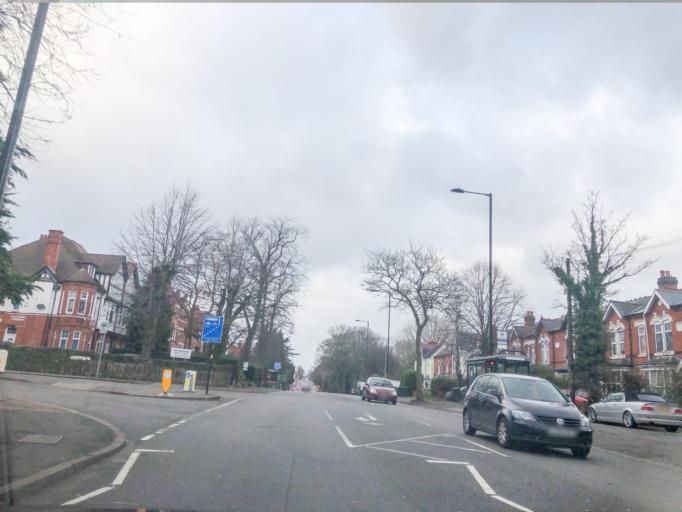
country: GB
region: England
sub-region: City and Borough of Birmingham
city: Birmingham
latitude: 52.4254
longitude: -1.8925
